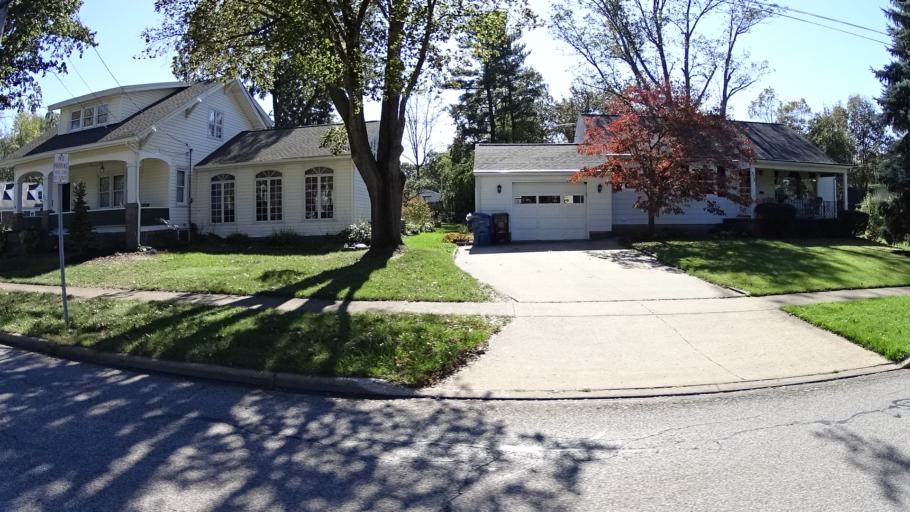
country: US
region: Ohio
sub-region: Lorain County
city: Amherst
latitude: 41.3983
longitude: -82.2161
